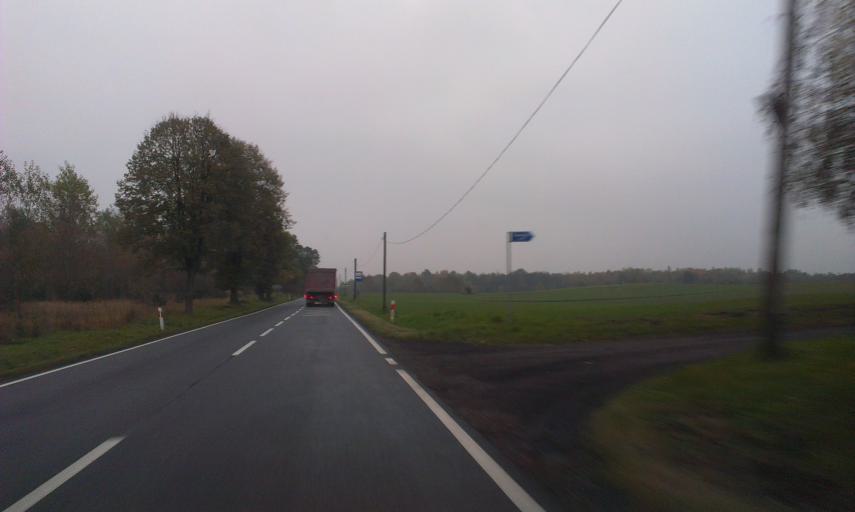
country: PL
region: Kujawsko-Pomorskie
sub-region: Powiat sepolenski
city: Sosno
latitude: 53.4384
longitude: 17.6266
